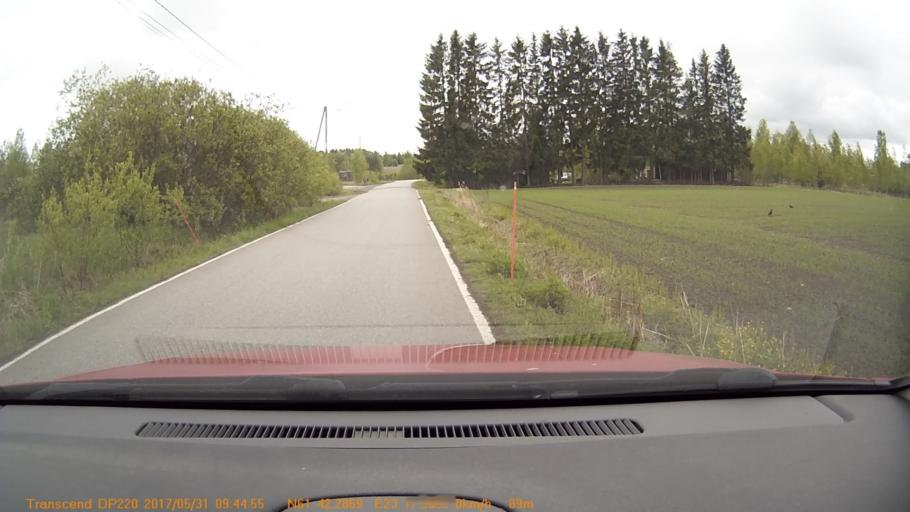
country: FI
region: Pirkanmaa
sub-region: Tampere
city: Viljakkala
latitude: 61.7048
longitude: 23.2882
